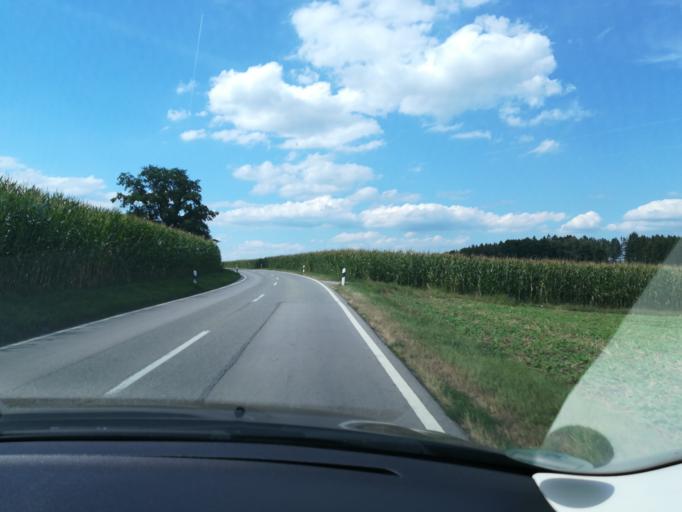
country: DE
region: Bavaria
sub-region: Upper Bavaria
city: Assling
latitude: 47.9596
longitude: 11.9686
